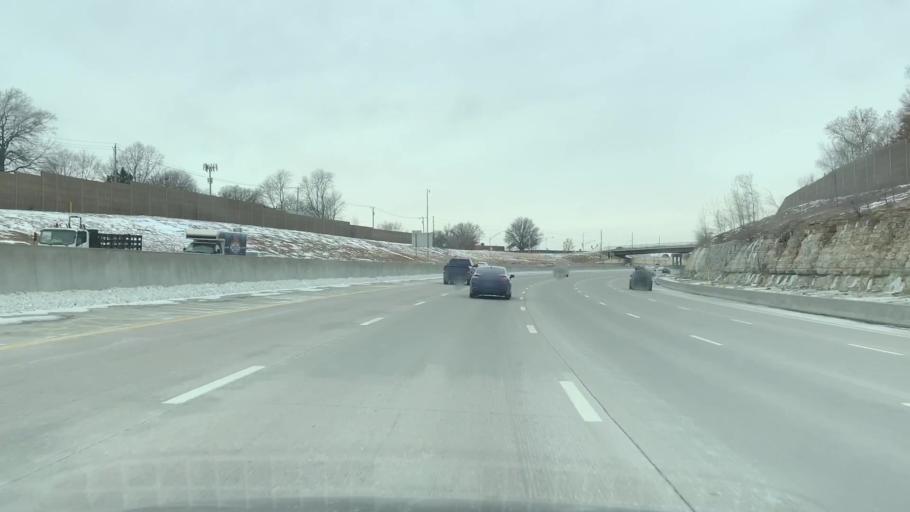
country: US
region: Kansas
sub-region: Johnson County
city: Lenexa
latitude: 38.9610
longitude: -94.7124
